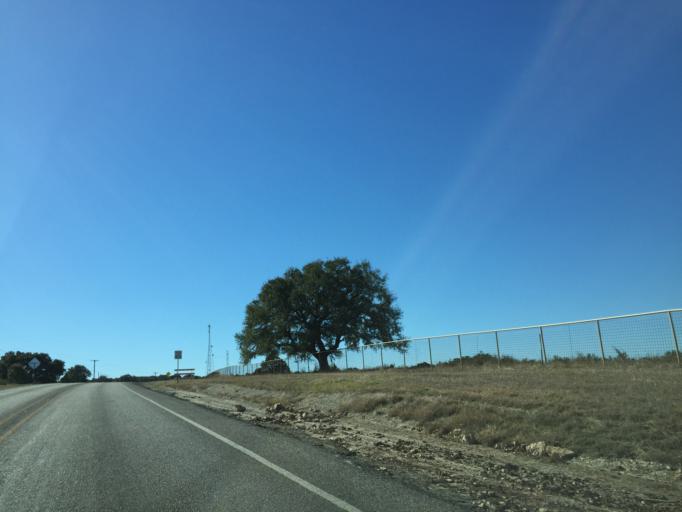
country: US
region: Texas
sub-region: Comal County
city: Canyon Lake
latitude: 29.7721
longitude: -98.2978
